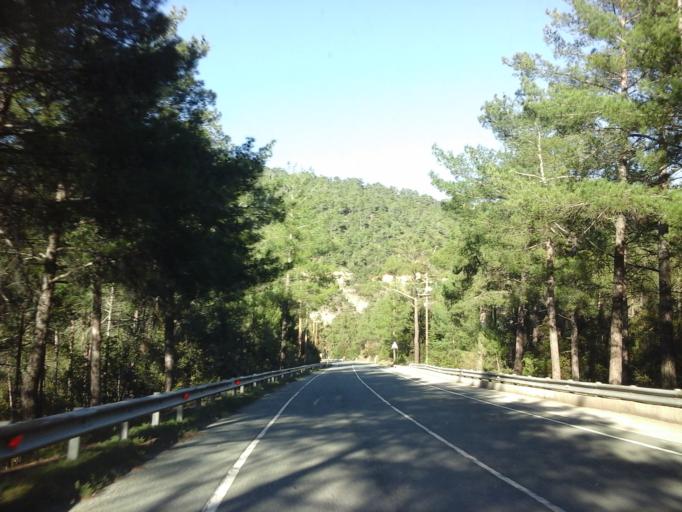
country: CY
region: Lefkosia
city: Kakopetria
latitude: 34.9607
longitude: 32.9237
